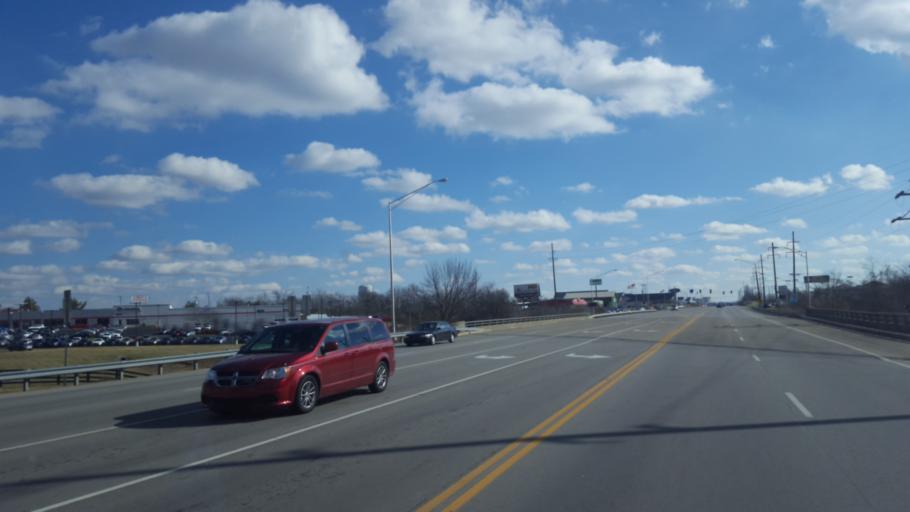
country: US
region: Kentucky
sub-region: Franklin County
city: Frankfort
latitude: 38.1883
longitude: -84.8215
